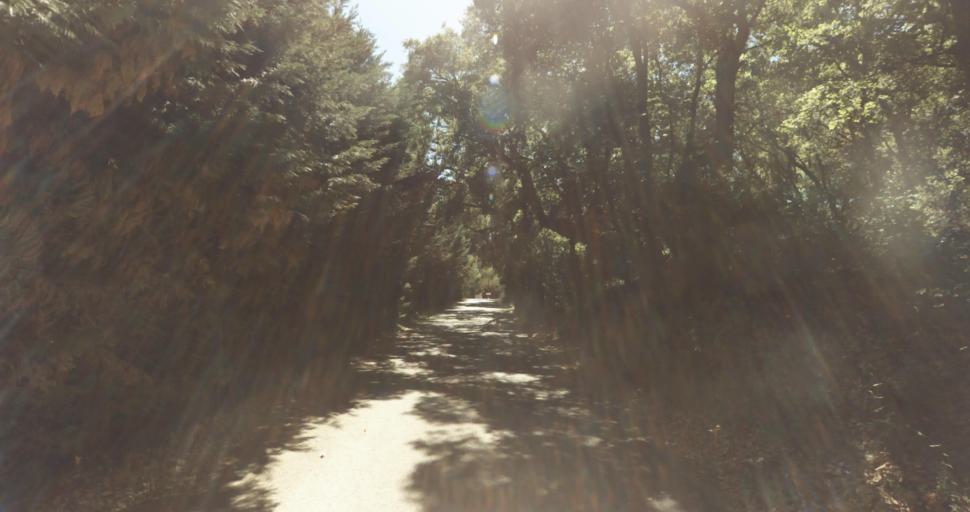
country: FR
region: Provence-Alpes-Cote d'Azur
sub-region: Departement du Var
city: Gassin
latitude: 43.2299
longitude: 6.5713
